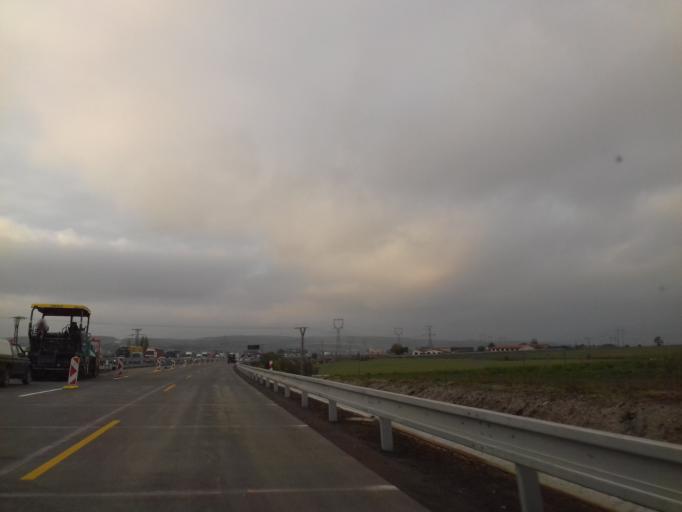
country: CZ
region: South Moravian
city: Ricany
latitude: 49.2003
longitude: 16.4238
